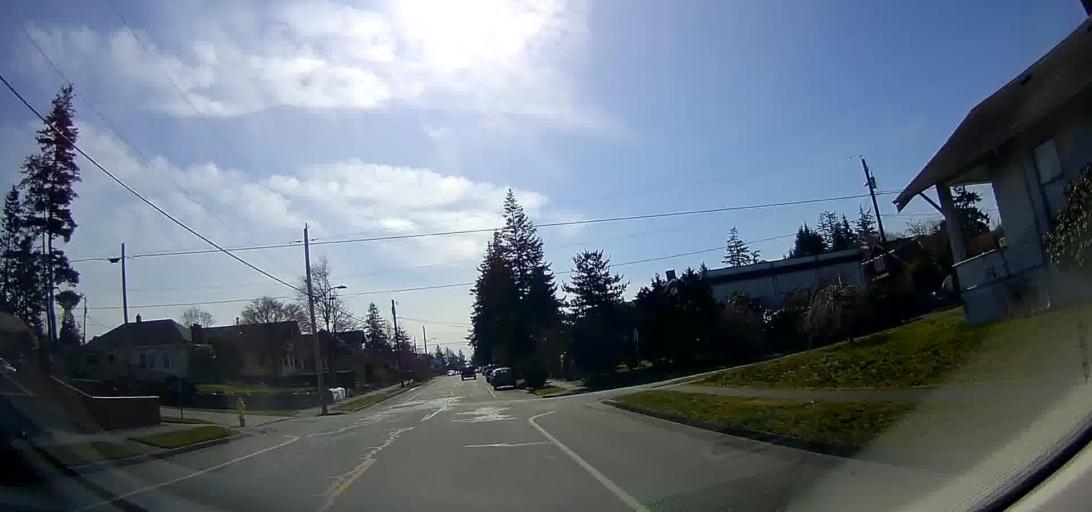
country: US
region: Washington
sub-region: Skagit County
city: Mount Vernon
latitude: 48.4254
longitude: -122.3331
